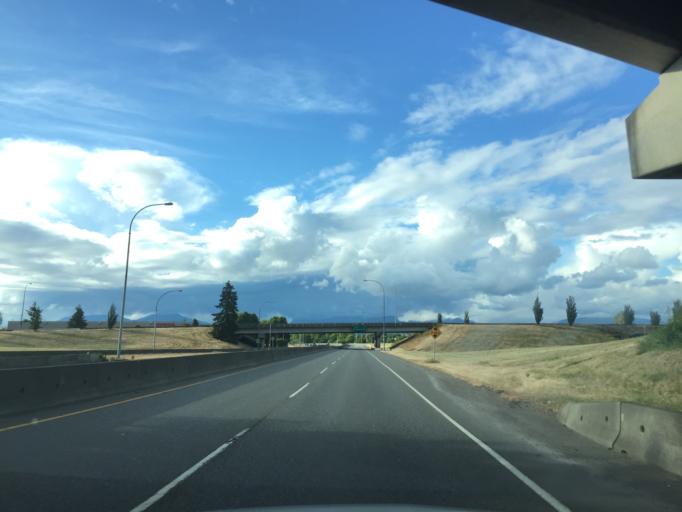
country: CA
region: British Columbia
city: Richmond
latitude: 49.1756
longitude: -123.0744
